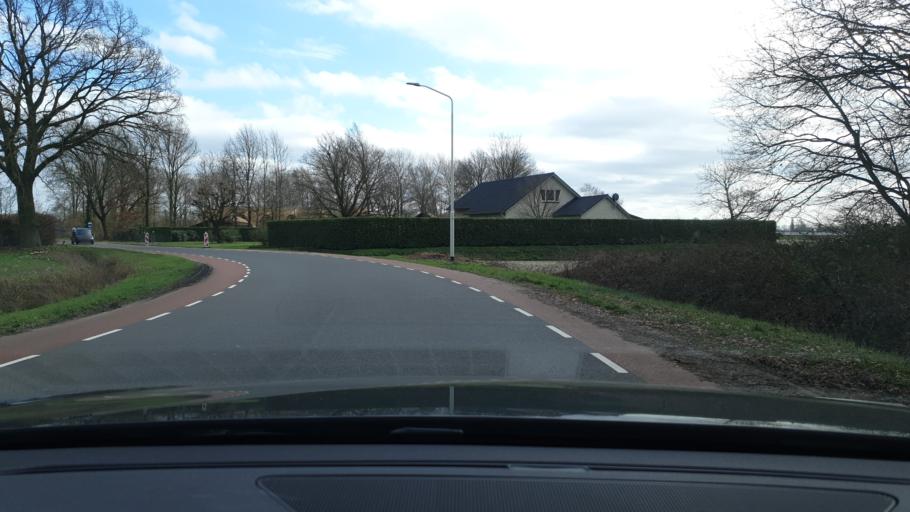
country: NL
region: North Brabant
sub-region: Gemeente Someren
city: Someren
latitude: 51.3874
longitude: 5.6747
